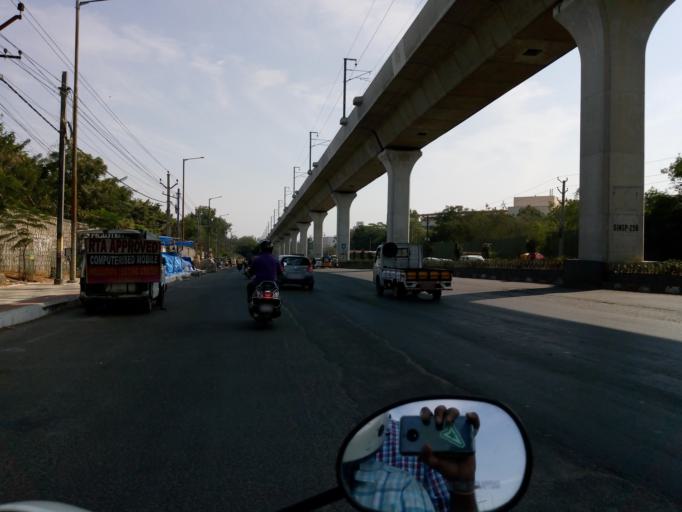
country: IN
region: Telangana
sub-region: Rangareddi
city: Uppal Kalan
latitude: 17.4135
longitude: 78.5478
